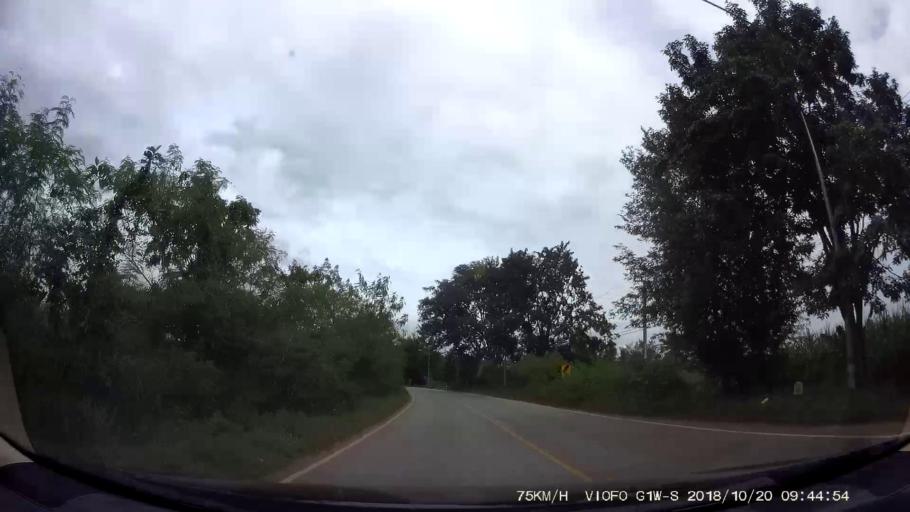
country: TH
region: Chaiyaphum
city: Khon San
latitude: 16.4879
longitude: 101.9417
